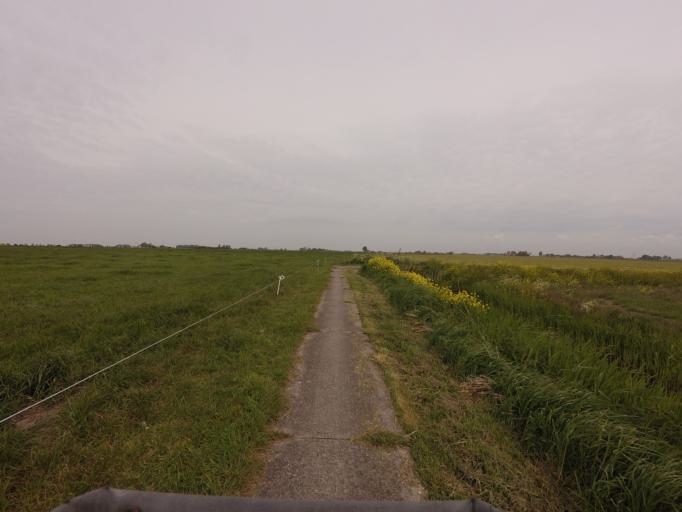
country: NL
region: Friesland
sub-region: Sudwest Fryslan
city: Workum
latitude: 53.0150
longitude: 5.4526
